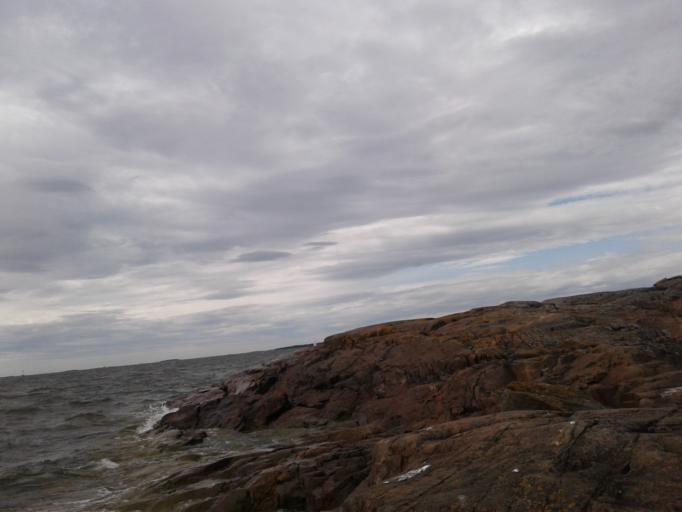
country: FI
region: Uusimaa
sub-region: Helsinki
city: Helsinki
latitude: 60.1461
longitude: 24.9746
